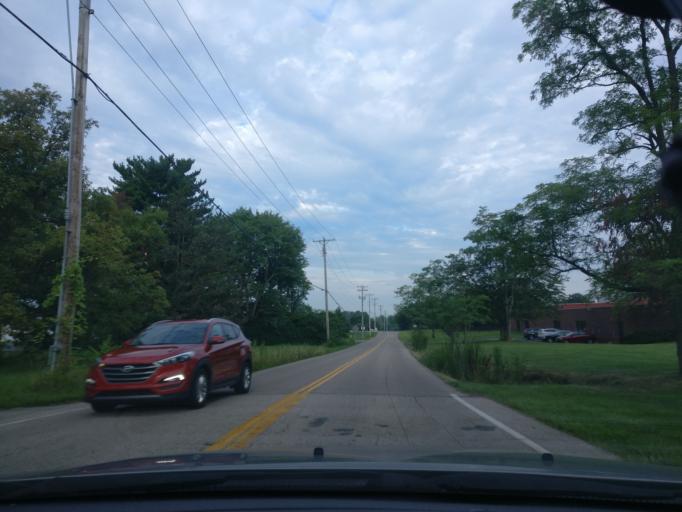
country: US
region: Ohio
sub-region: Montgomery County
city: West Carrollton City
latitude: 39.6298
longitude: -84.2360
